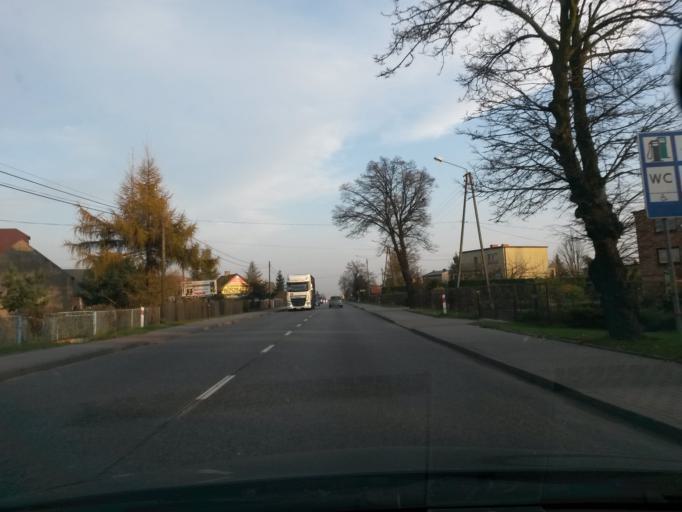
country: PL
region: Lodz Voivodeship
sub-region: Powiat wielunski
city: Wielun
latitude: 51.2302
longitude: 18.5448
